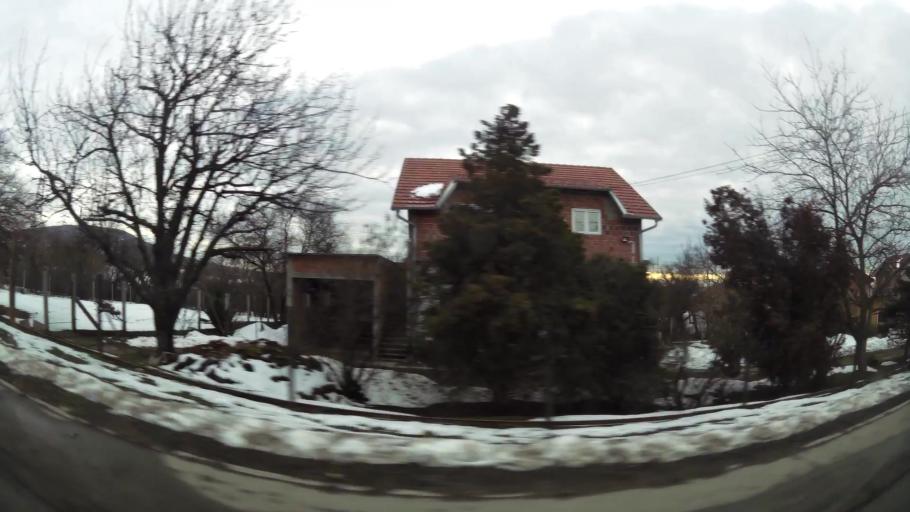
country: RS
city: Rusanj
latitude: 44.7213
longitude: 20.4995
